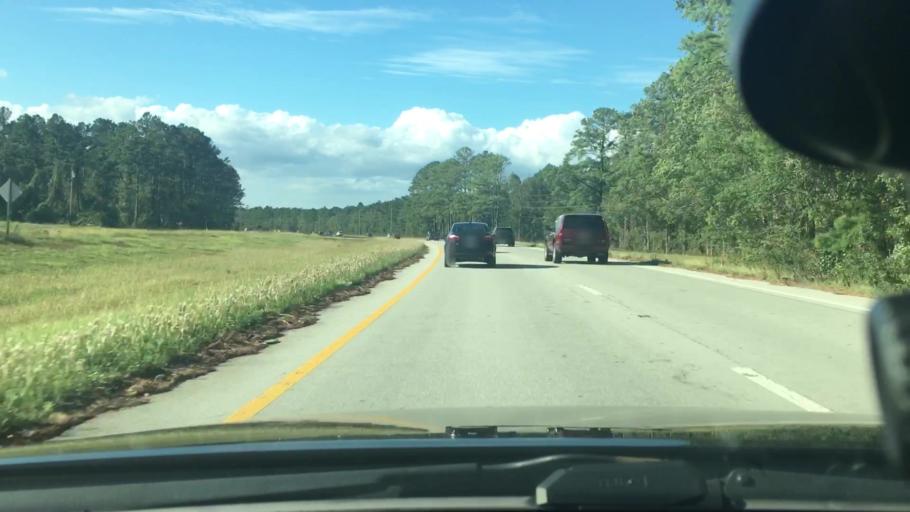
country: US
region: North Carolina
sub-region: Craven County
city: Neuse Forest
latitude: 34.9576
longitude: -76.9507
